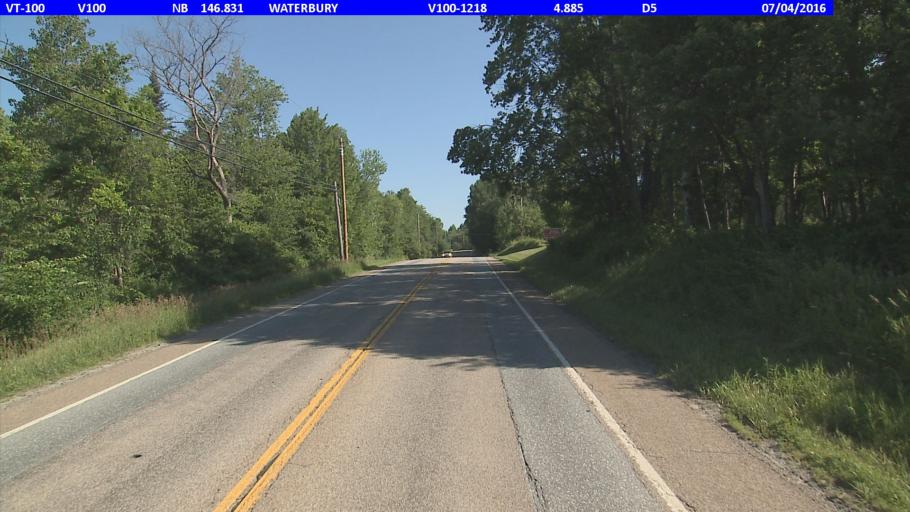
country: US
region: Vermont
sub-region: Washington County
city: Waterbury
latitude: 44.3996
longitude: -72.7191
